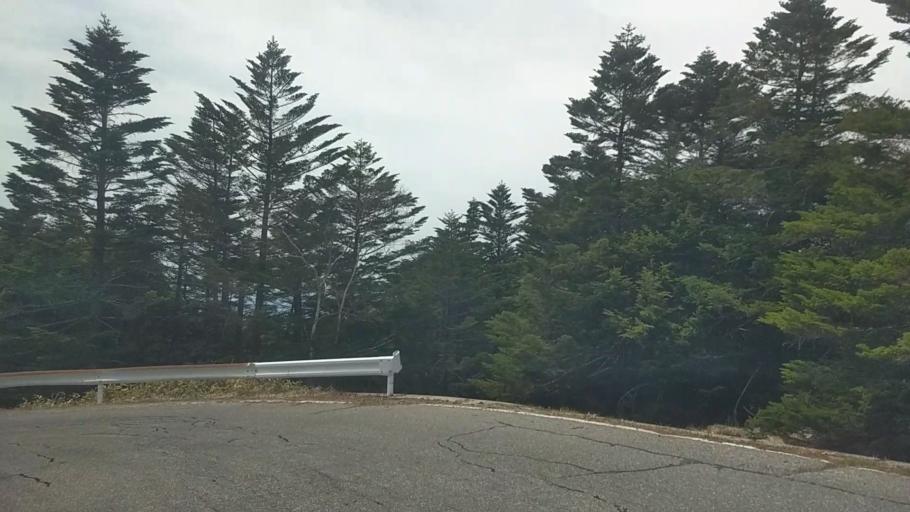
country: JP
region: Nagano
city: Chino
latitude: 36.0585
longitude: 138.3249
